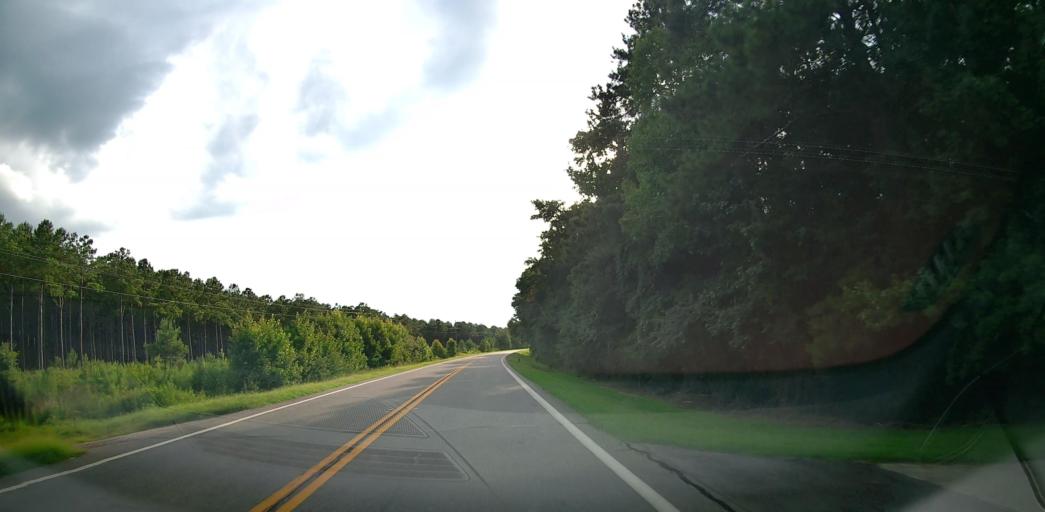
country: US
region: Georgia
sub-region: Pulaski County
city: Hawkinsville
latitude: 32.2956
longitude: -83.5580
